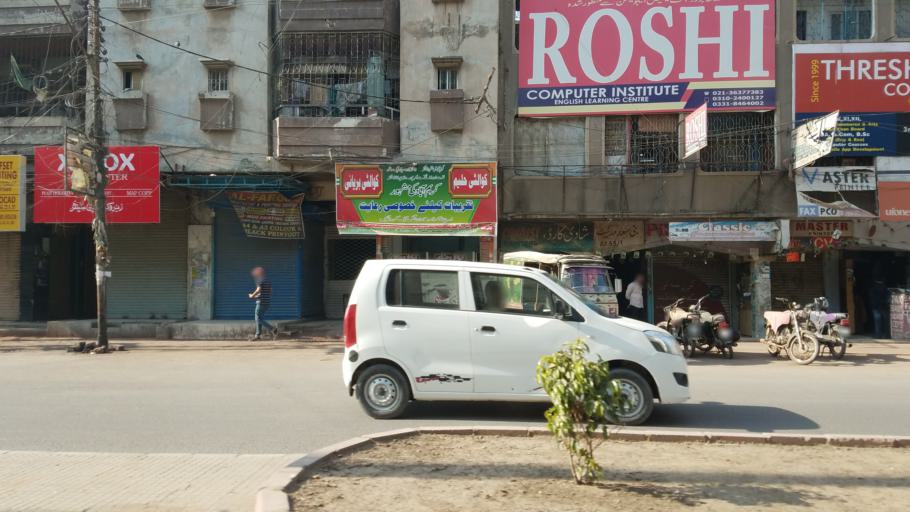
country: PK
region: Sindh
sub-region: Karachi District
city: Karachi
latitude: 24.9177
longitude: 67.0543
